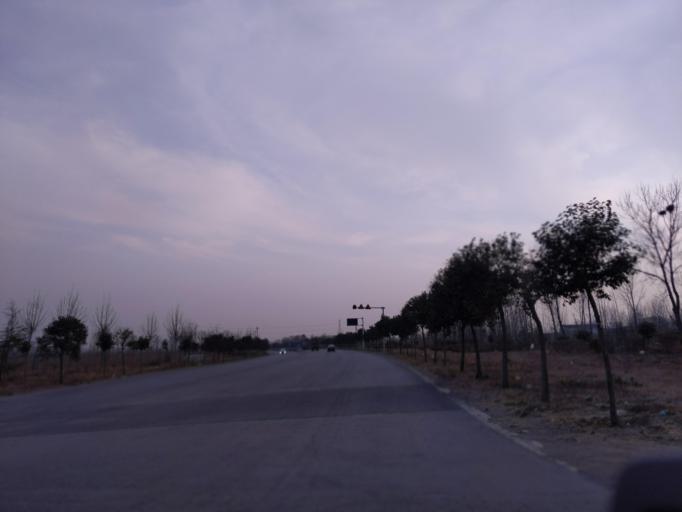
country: CN
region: Henan Sheng
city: Puyang
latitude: 35.8135
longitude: 114.9670
